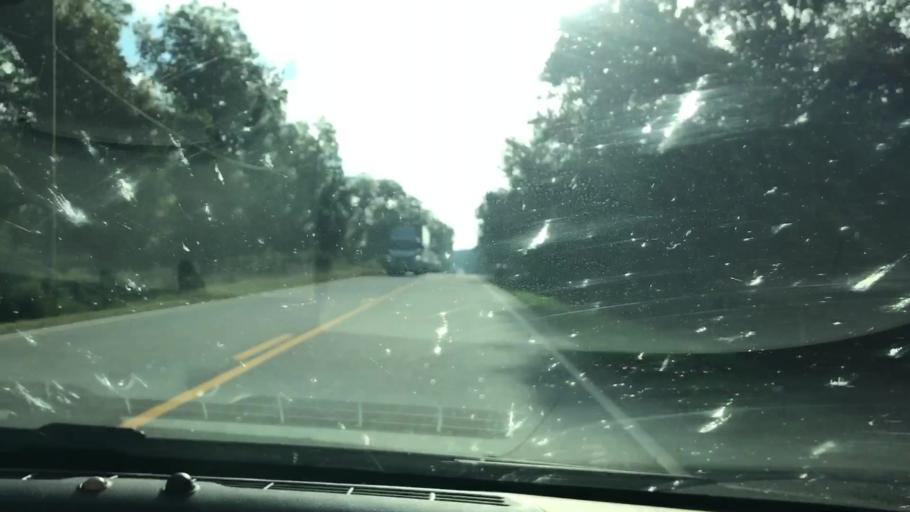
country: US
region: Georgia
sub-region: Terrell County
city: Dawson
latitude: 31.7702
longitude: -84.5220
